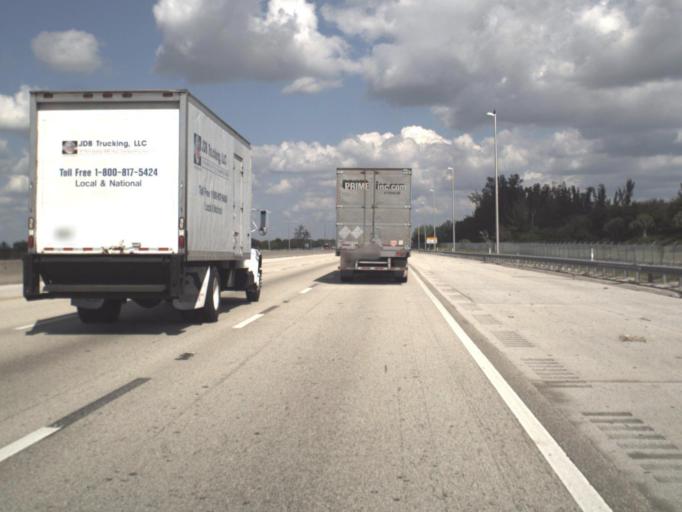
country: US
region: Florida
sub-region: Palm Beach County
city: Villages of Oriole
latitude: 26.5392
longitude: -80.1726
